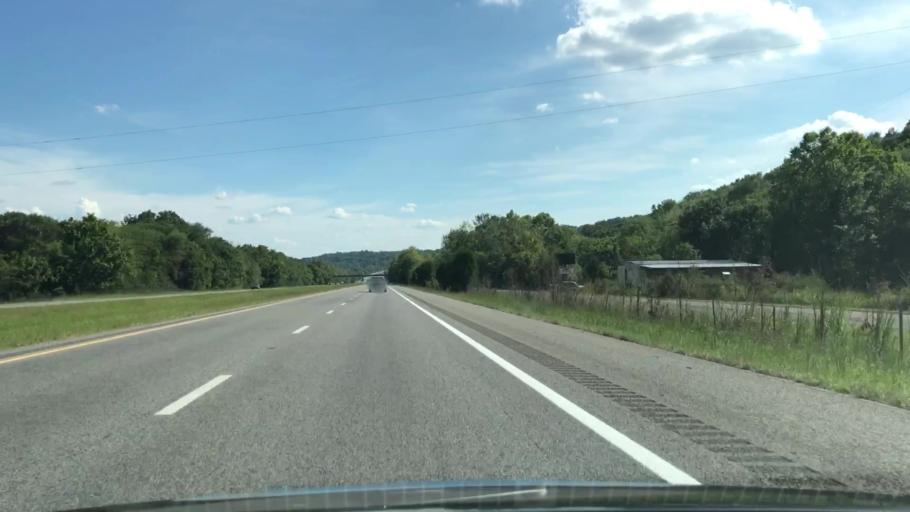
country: US
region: Alabama
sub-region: Limestone County
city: Ardmore
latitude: 35.1447
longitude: -86.8788
